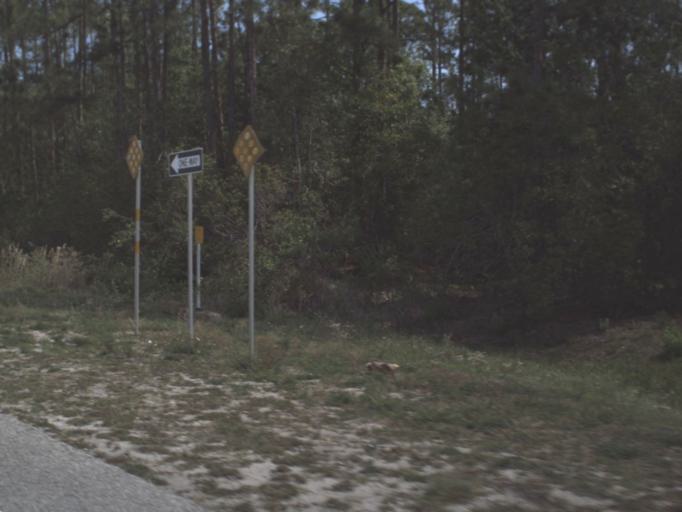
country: US
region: Florida
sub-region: Flagler County
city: Bunnell
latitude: 29.5108
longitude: -81.2639
